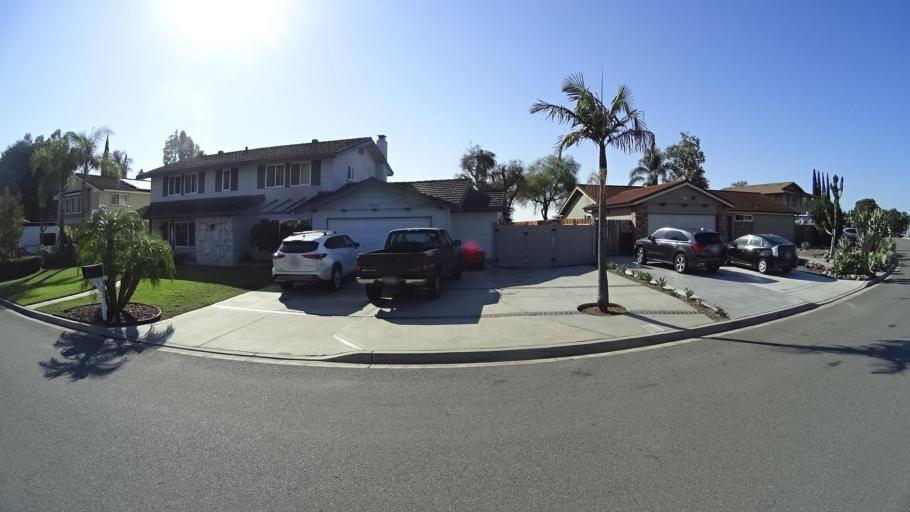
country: US
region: California
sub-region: San Diego County
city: Casa de Oro-Mount Helix
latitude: 32.7623
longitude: -116.9882
